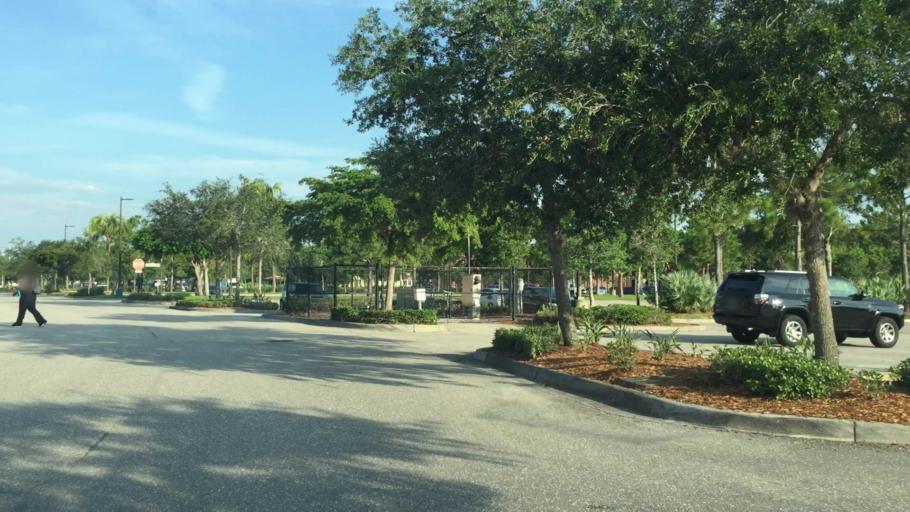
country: US
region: Florida
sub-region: Lee County
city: Estero
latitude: 26.4073
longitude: -81.8081
